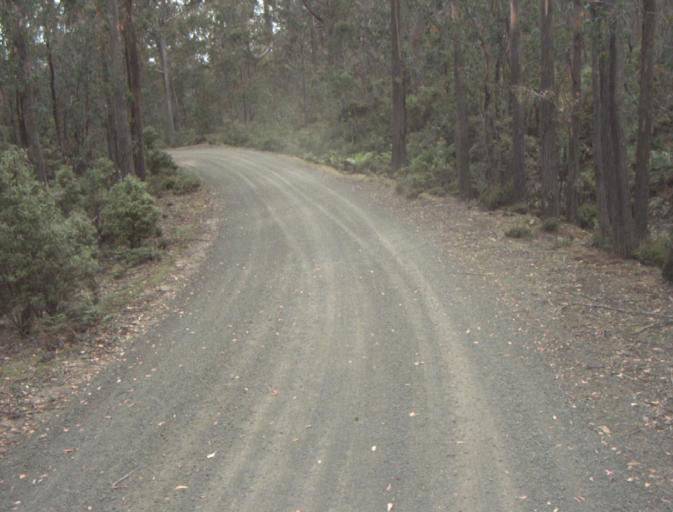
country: AU
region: Tasmania
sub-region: Dorset
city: Scottsdale
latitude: -41.5014
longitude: 147.6070
